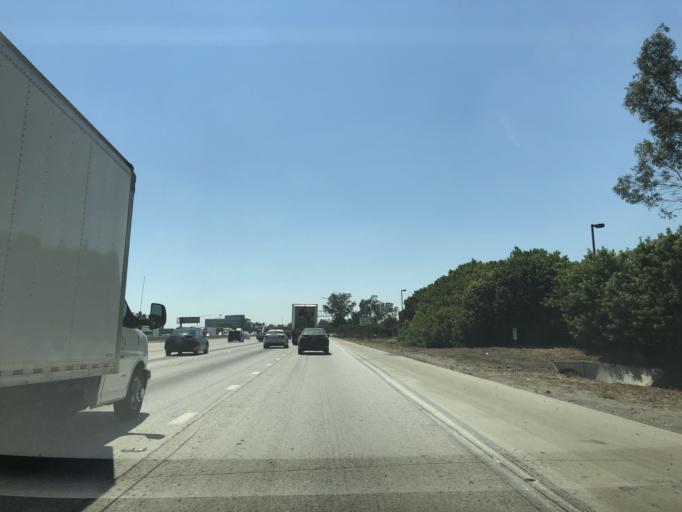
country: US
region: California
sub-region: San Bernardino County
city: Rancho Cucamonga
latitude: 34.0678
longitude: -117.5695
